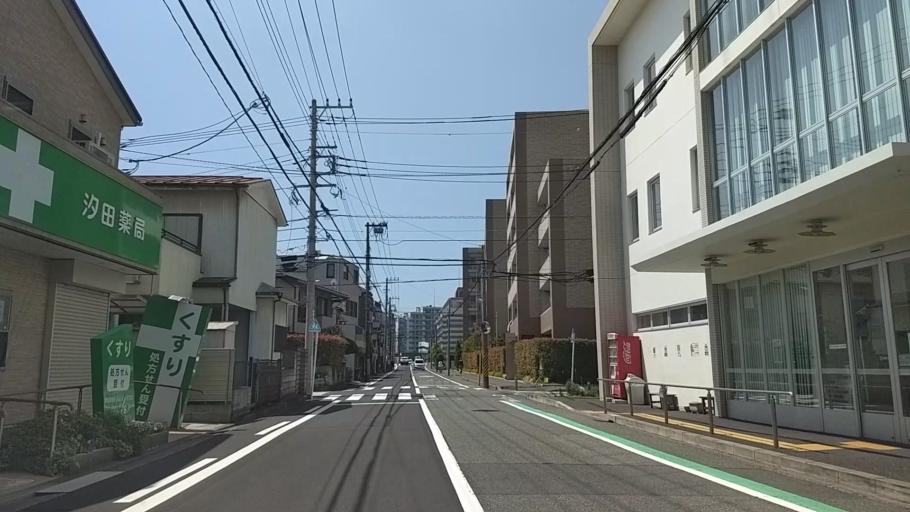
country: JP
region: Kanagawa
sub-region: Kawasaki-shi
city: Kawasaki
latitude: 35.5023
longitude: 139.6799
